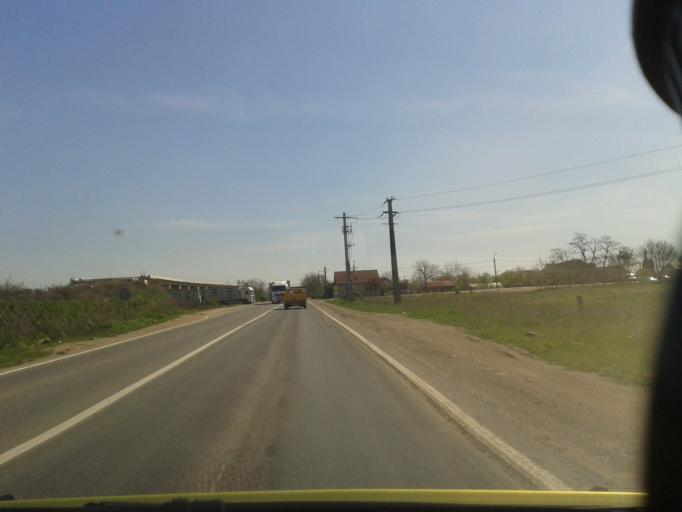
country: RO
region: Arad
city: Arad
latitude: 46.2159
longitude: 21.3186
